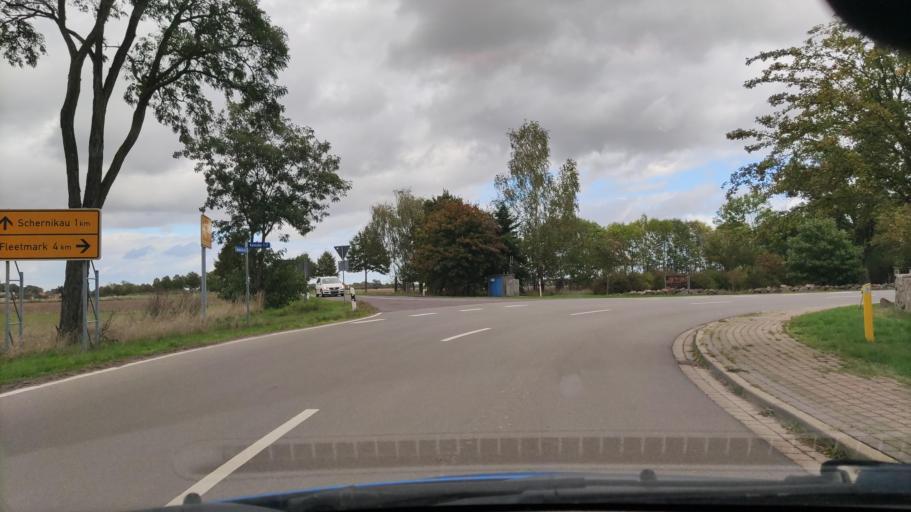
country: DE
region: Saxony-Anhalt
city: Pretzier
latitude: 52.8220
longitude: 11.3788
